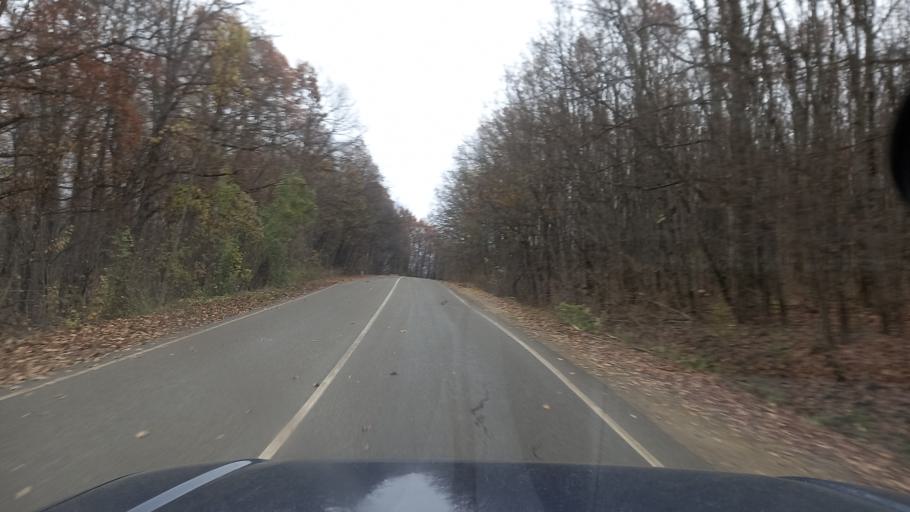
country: RU
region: Krasnodarskiy
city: Goryachiy Klyuch
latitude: 44.5484
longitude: 39.2522
